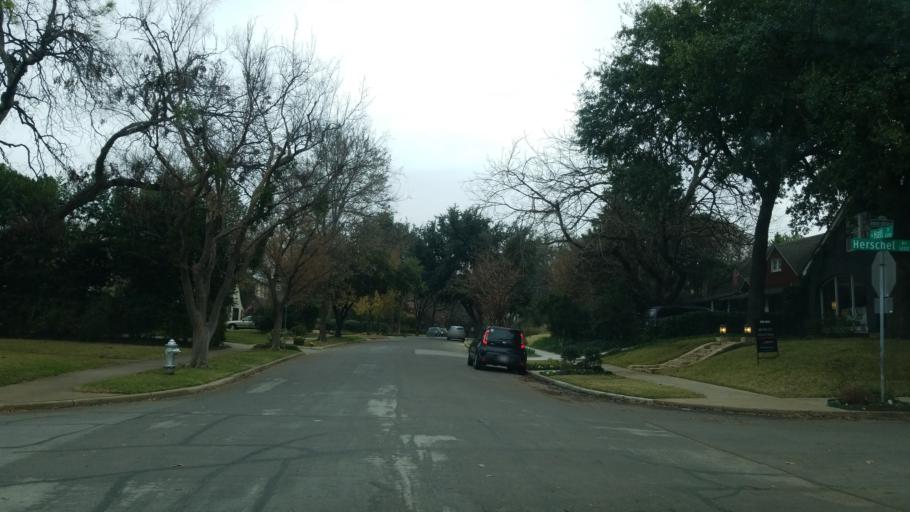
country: US
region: Texas
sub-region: Dallas County
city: Highland Park
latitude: 32.8164
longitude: -96.8145
